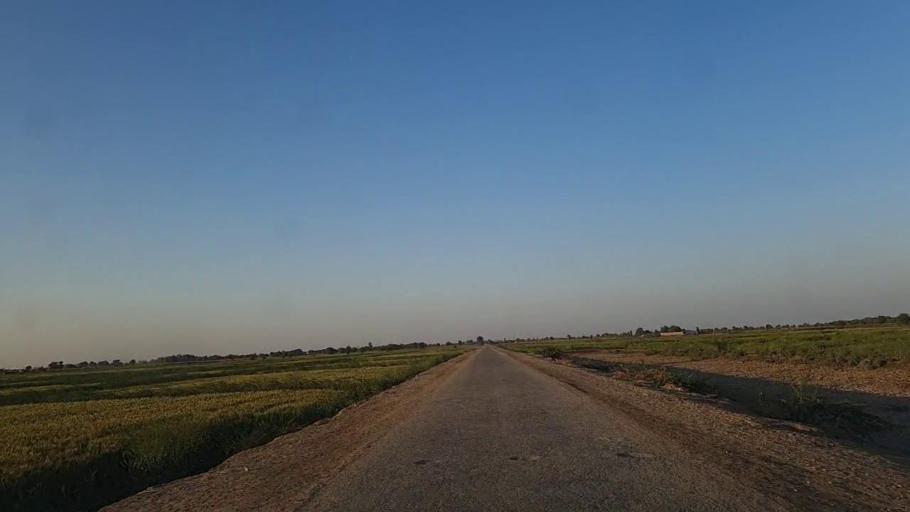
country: PK
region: Sindh
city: Naukot
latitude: 25.0227
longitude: 69.4168
